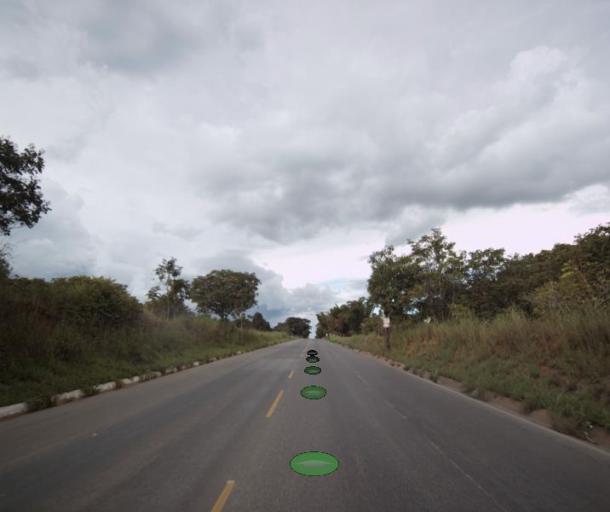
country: BR
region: Goias
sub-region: Itapaci
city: Itapaci
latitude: -15.0754
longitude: -49.4598
